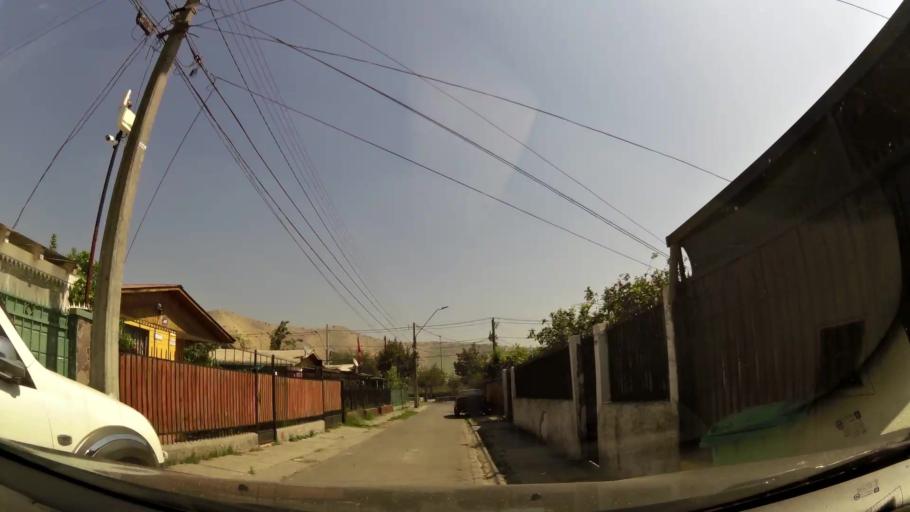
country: CL
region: Santiago Metropolitan
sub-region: Provincia de Maipo
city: San Bernardo
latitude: -33.5835
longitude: -70.7129
